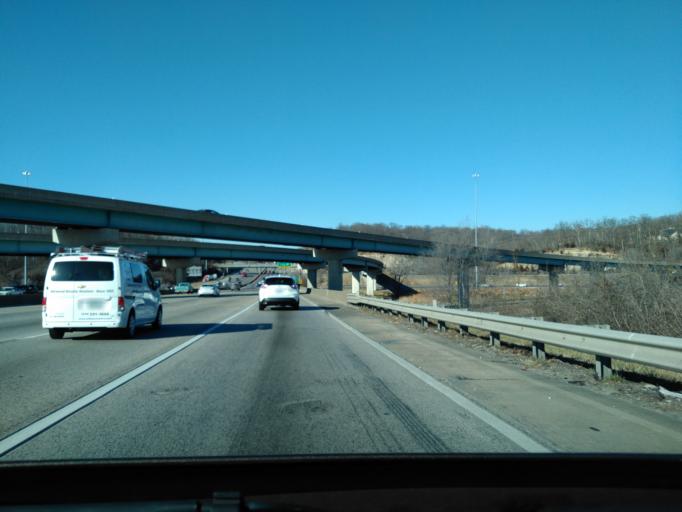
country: US
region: Missouri
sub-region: Saint Louis County
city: Sunset Hills
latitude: 38.5480
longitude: -90.4262
